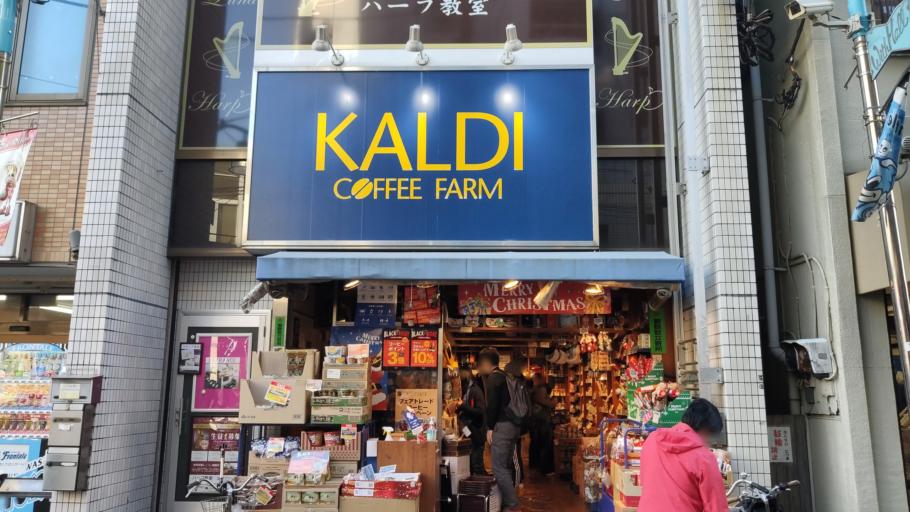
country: JP
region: Kanagawa
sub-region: Kawasaki-shi
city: Kawasaki
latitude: 35.5804
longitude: 139.6616
